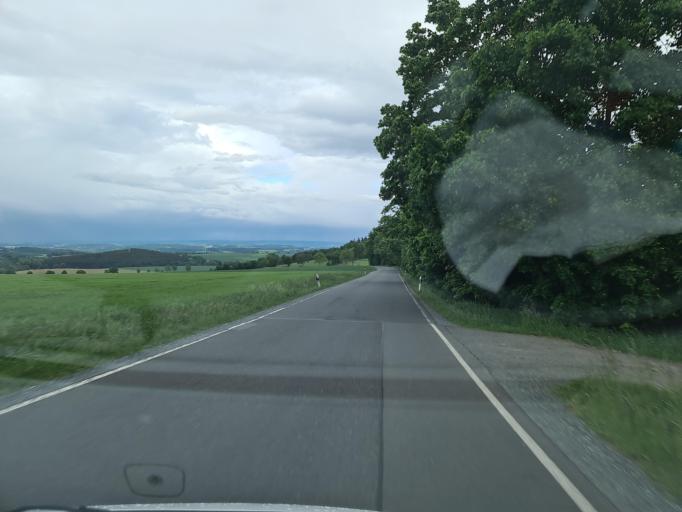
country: DE
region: Saxony
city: Reuth
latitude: 50.4721
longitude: 11.9782
